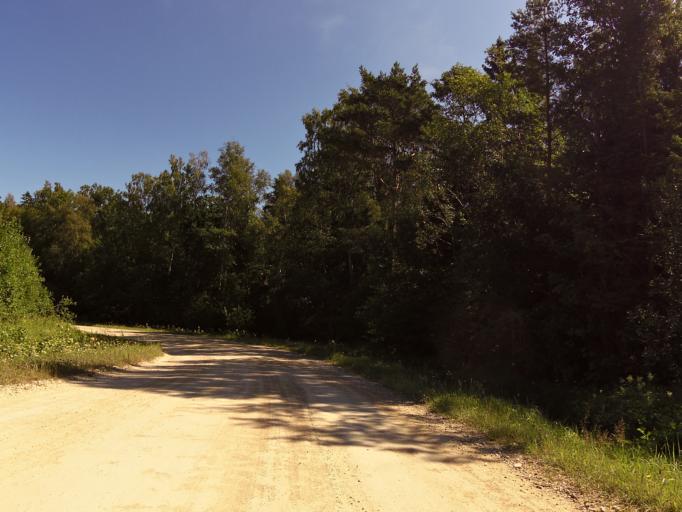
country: EE
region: Hiiumaa
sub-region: Kaerdla linn
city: Kardla
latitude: 58.9282
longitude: 22.3708
